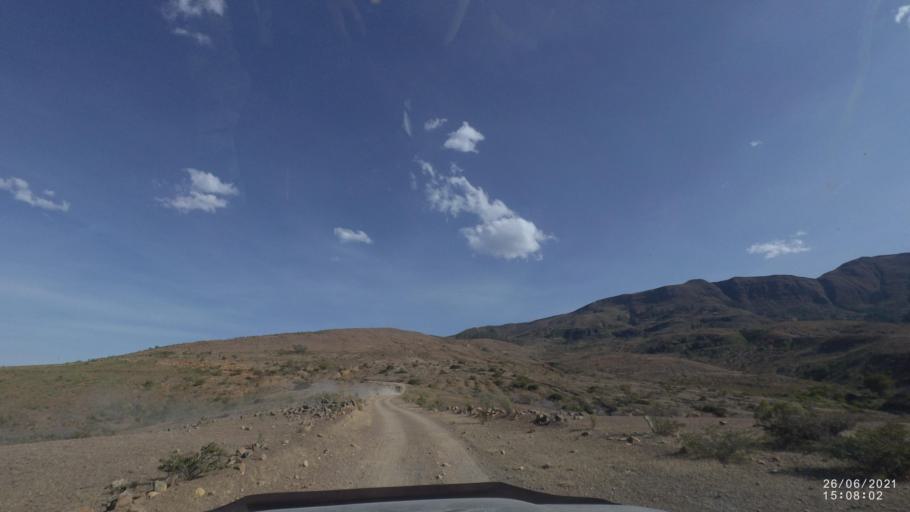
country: BO
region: Cochabamba
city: Mizque
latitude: -17.9459
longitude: -65.6399
